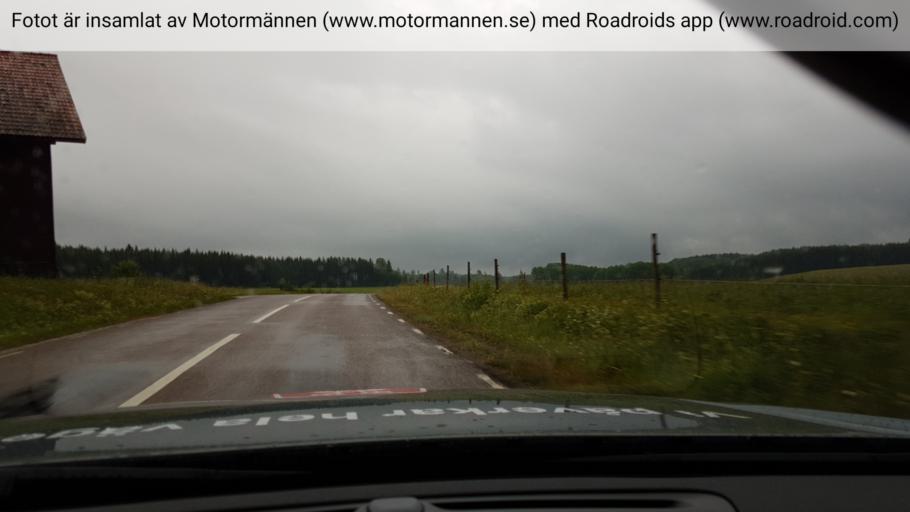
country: SE
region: Dalarna
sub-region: Avesta Kommun
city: Avesta
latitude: 59.9976
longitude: 16.0870
